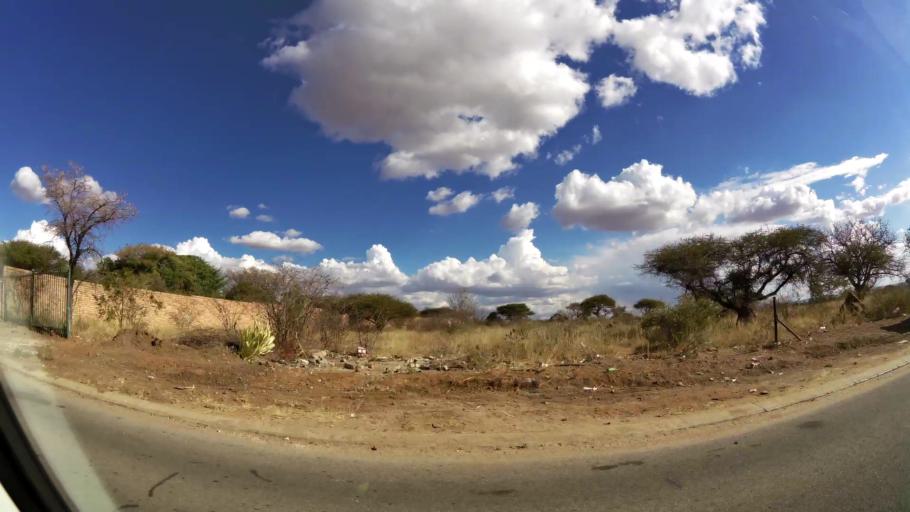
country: ZA
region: Limpopo
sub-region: Capricorn District Municipality
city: Polokwane
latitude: -23.8767
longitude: 29.4840
